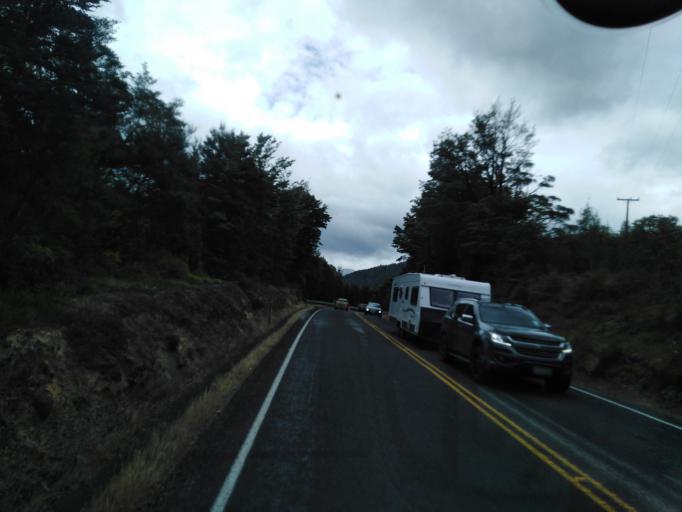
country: NZ
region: Tasman
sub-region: Tasman District
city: Wakefield
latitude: -41.7070
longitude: 172.5414
